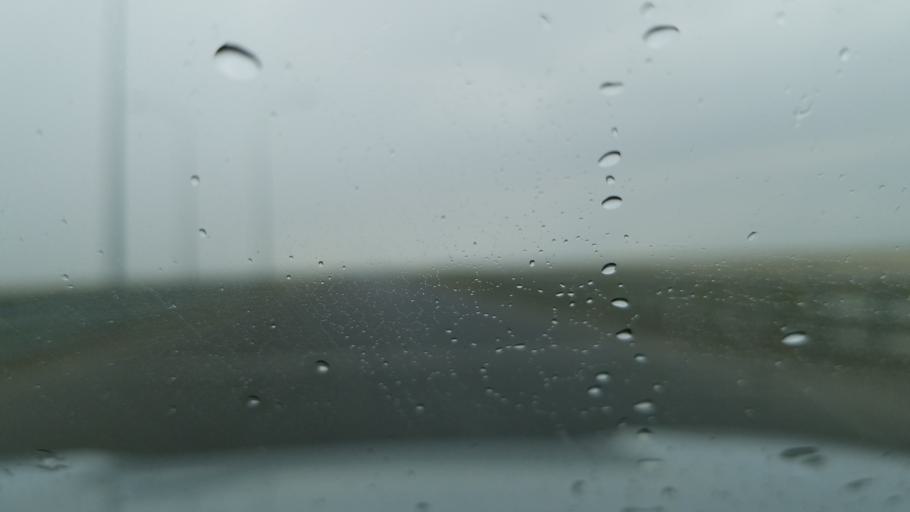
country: TM
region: Balkan
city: Serdar
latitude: 39.0096
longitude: 56.2396
